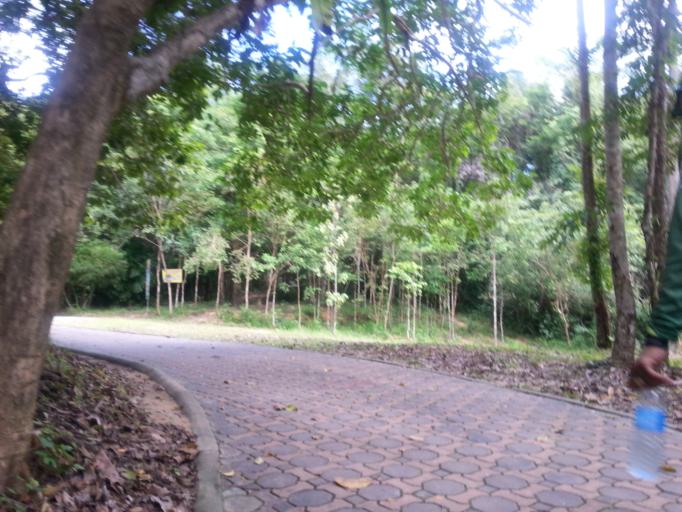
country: TH
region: Krabi
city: Khlong Thom
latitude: 7.9314
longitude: 99.2059
